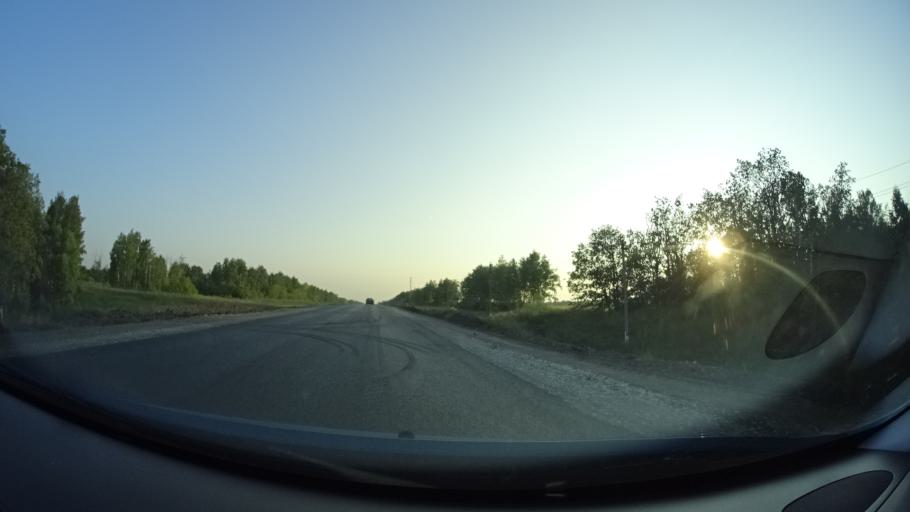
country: RU
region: Samara
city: Isakly
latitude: 53.9825
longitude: 51.4916
